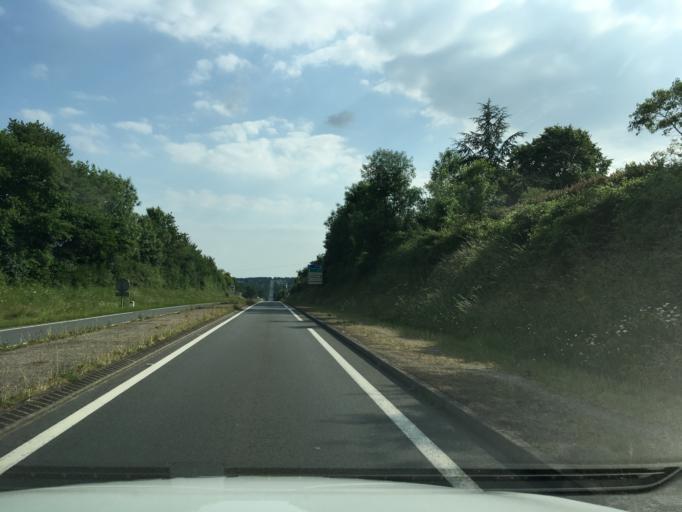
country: FR
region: Poitou-Charentes
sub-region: Departement des Deux-Sevres
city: Saint-Pardoux
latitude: 46.5715
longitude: -0.2970
